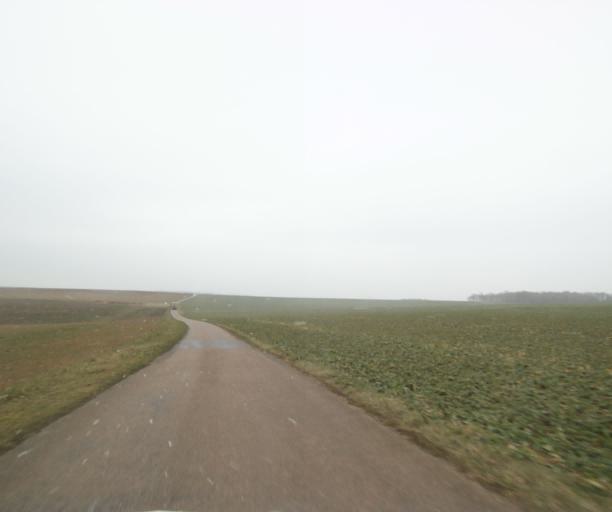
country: FR
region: Champagne-Ardenne
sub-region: Departement de la Haute-Marne
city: Chevillon
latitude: 48.5125
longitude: 5.0869
